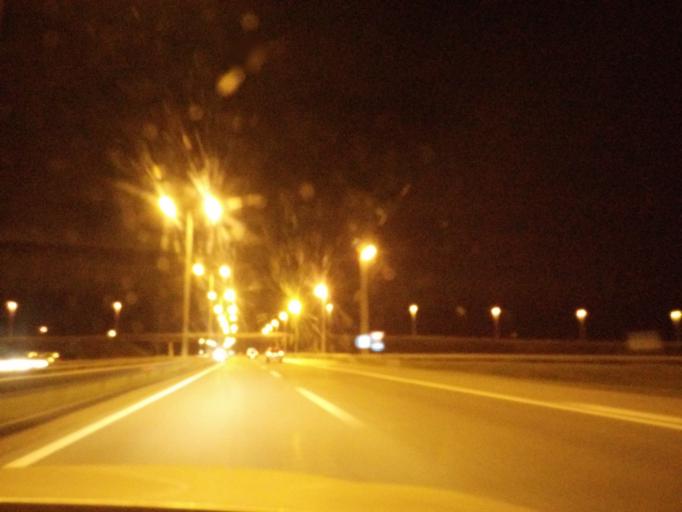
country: RS
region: Autonomna Pokrajina Vojvodina
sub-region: Sremski Okrug
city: Pecinci
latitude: 44.9230
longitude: 19.9533
